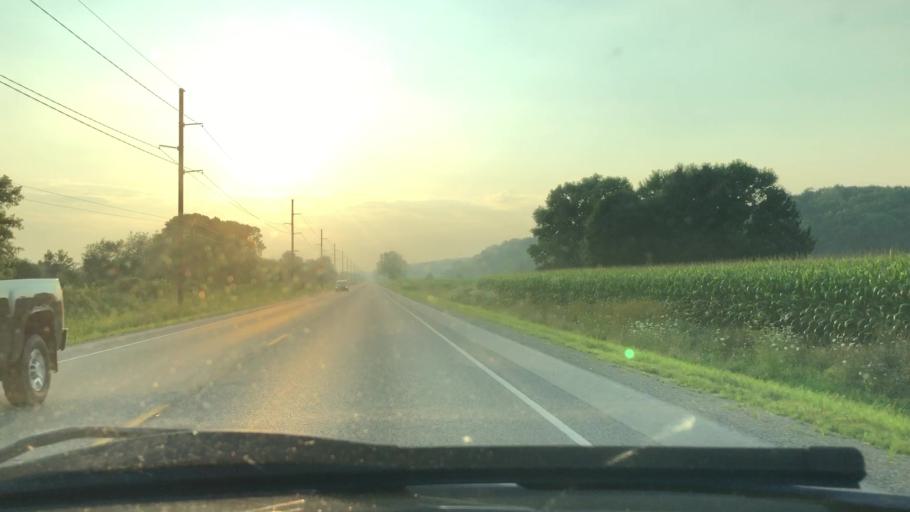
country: US
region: Wisconsin
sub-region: Dane County
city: Cross Plains
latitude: 43.1209
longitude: -89.6933
